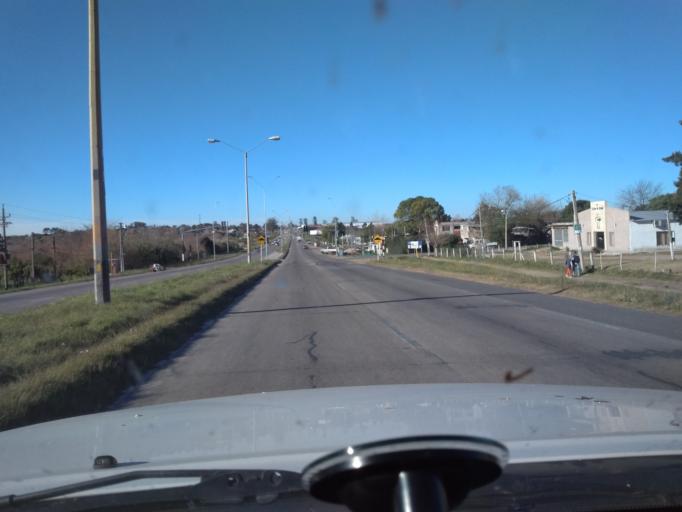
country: UY
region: Canelones
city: Colonia Nicolich
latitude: -34.7755
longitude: -56.0381
